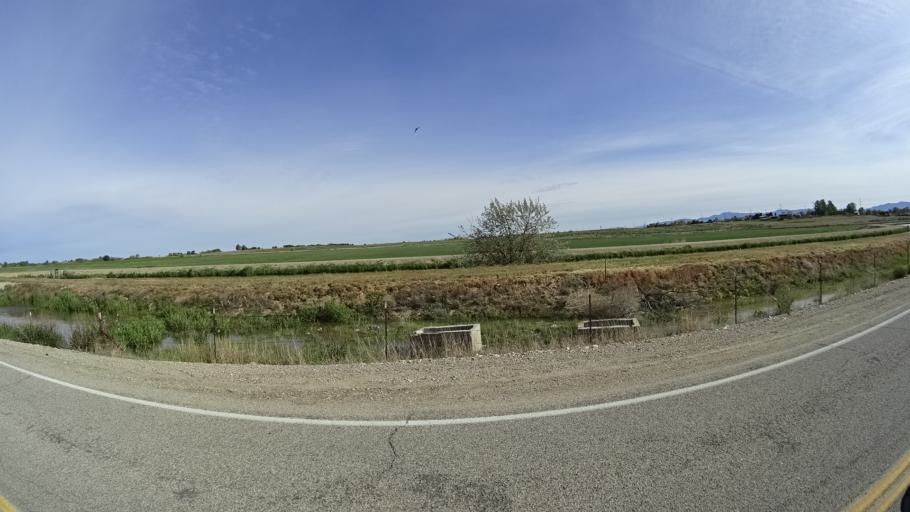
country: US
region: Idaho
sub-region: Ada County
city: Kuna
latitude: 43.4731
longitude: -116.3402
